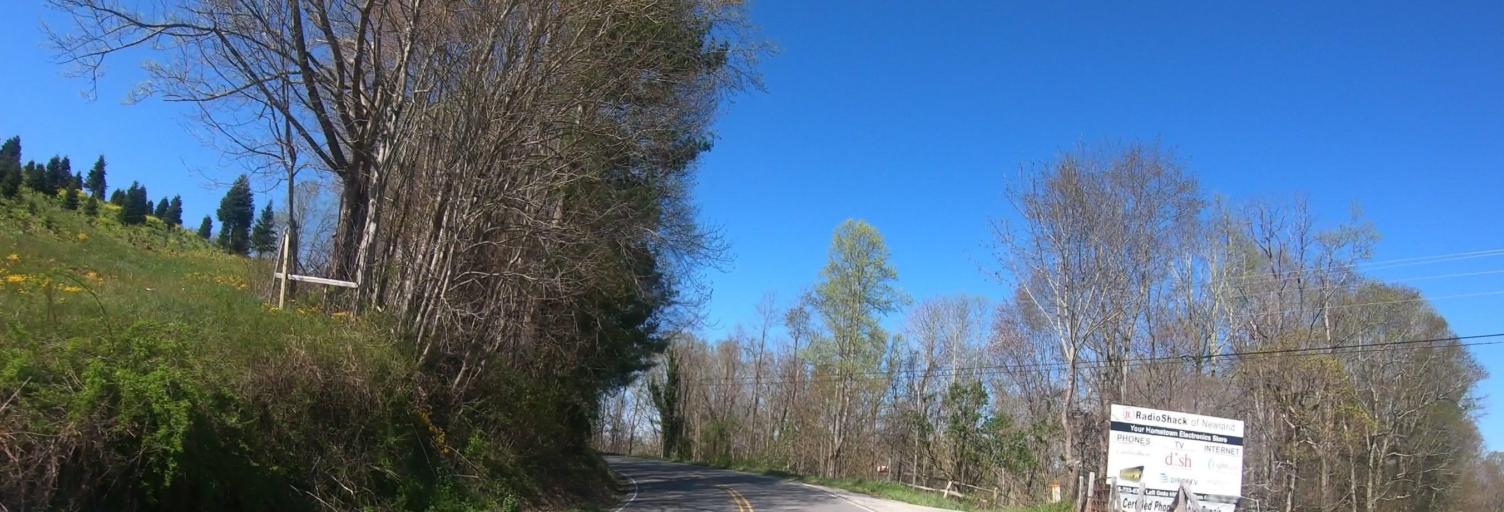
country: US
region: North Carolina
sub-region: Avery County
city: Newland
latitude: 35.9826
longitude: -81.9549
